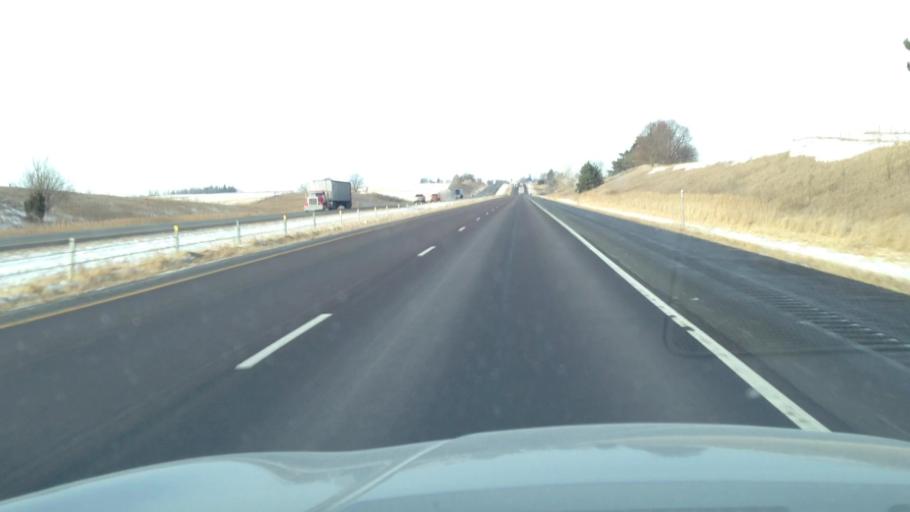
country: US
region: Iowa
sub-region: Poweshiek County
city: Grinnell
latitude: 41.6956
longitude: -92.6823
